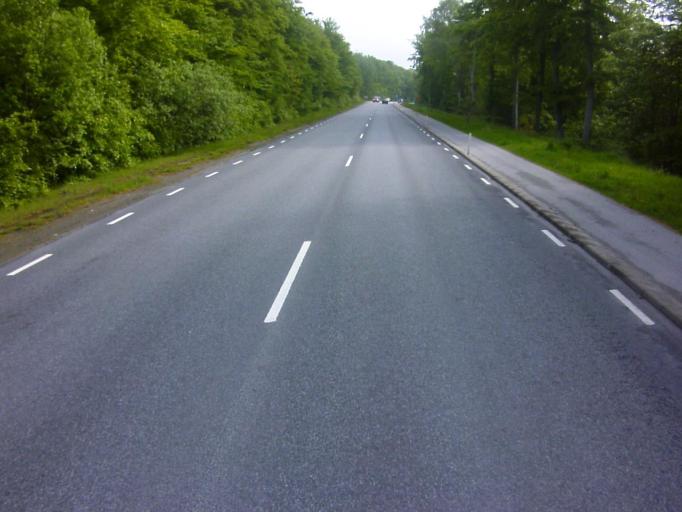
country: SE
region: Blekinge
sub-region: Solvesborgs Kommun
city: Soelvesborg
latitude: 56.0562
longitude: 14.5754
